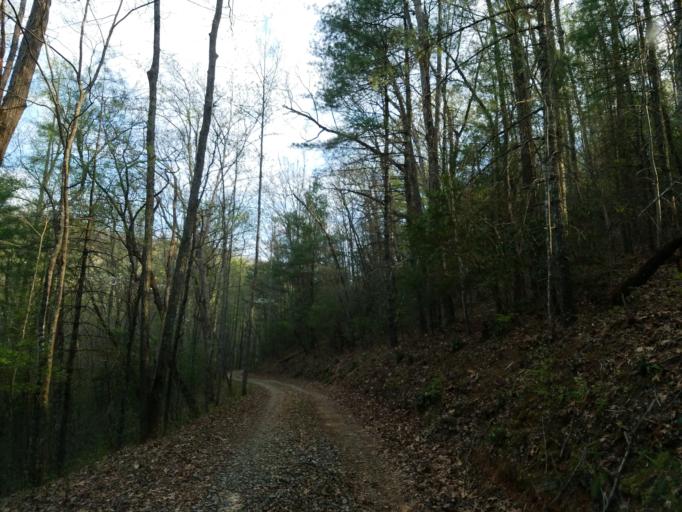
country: US
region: Georgia
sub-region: Fannin County
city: Blue Ridge
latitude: 34.7229
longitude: -84.2021
